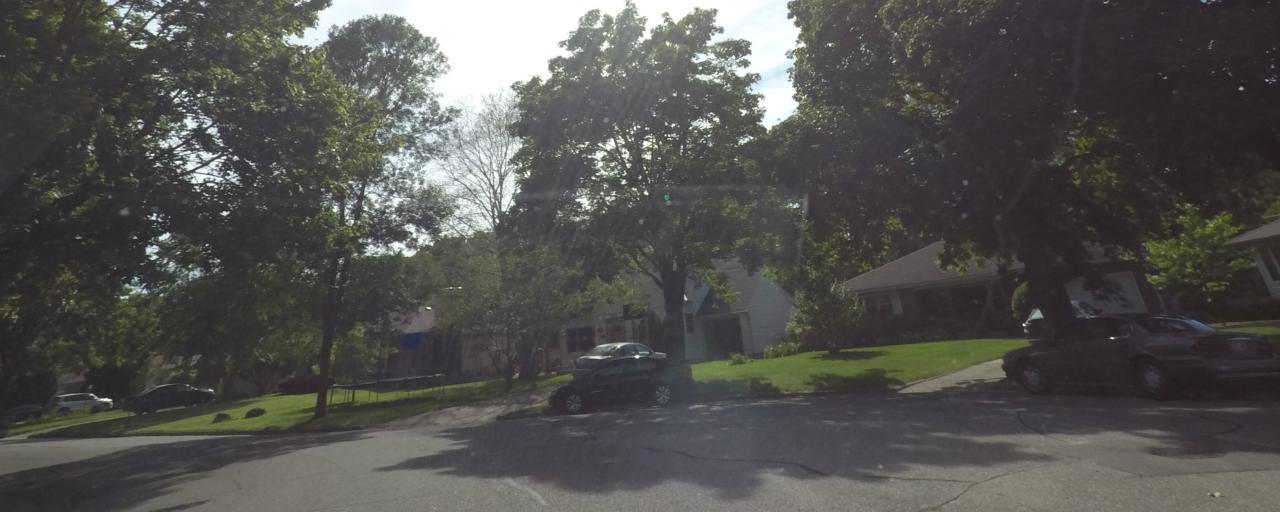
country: US
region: Wisconsin
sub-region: Dane County
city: Shorewood Hills
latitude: 43.0450
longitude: -89.4528
